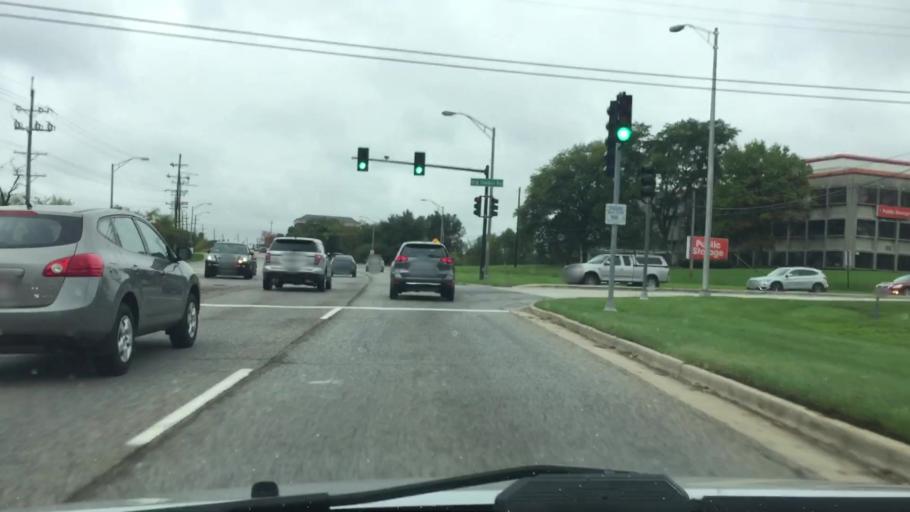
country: US
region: Illinois
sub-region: Kane County
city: Elgin
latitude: 42.0587
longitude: -88.2944
